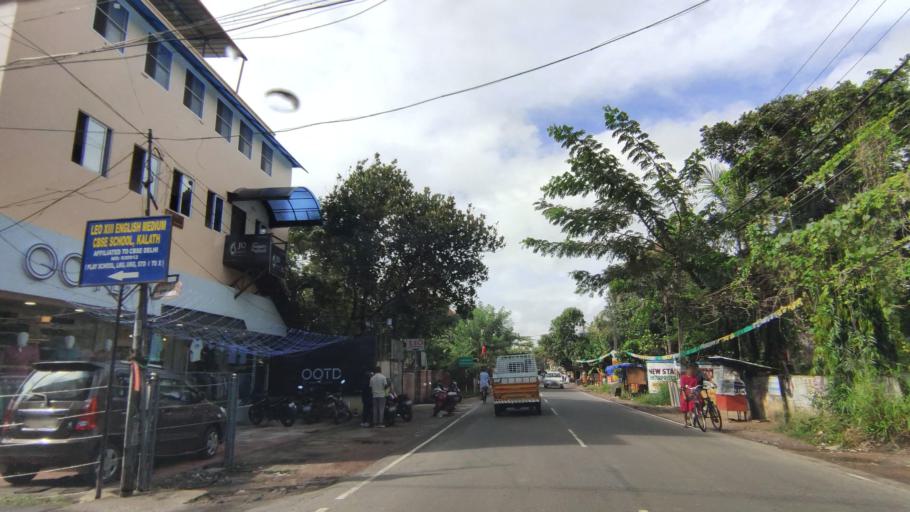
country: IN
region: Kerala
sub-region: Alappuzha
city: Alleppey
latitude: 9.5202
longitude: 76.3393
